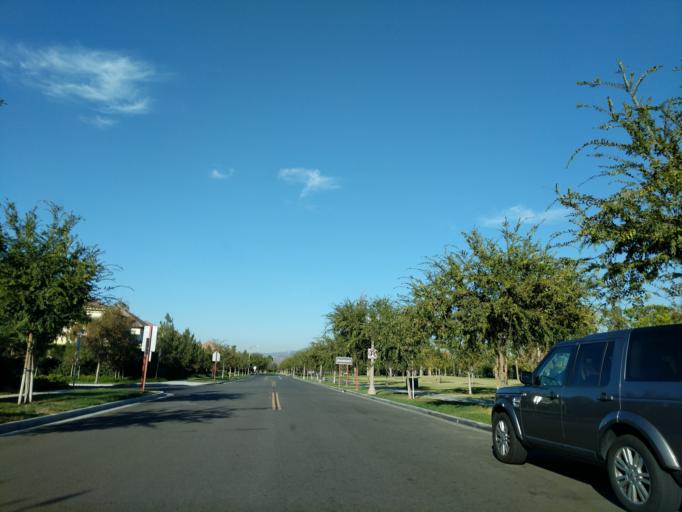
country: US
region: California
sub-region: Orange County
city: Irvine
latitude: 33.6873
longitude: -117.7585
